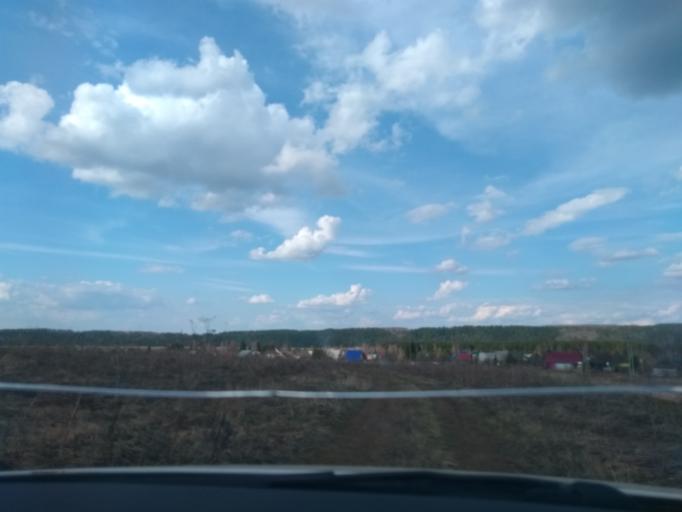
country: RU
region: Perm
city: Sylva
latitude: 57.8411
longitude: 56.7907
